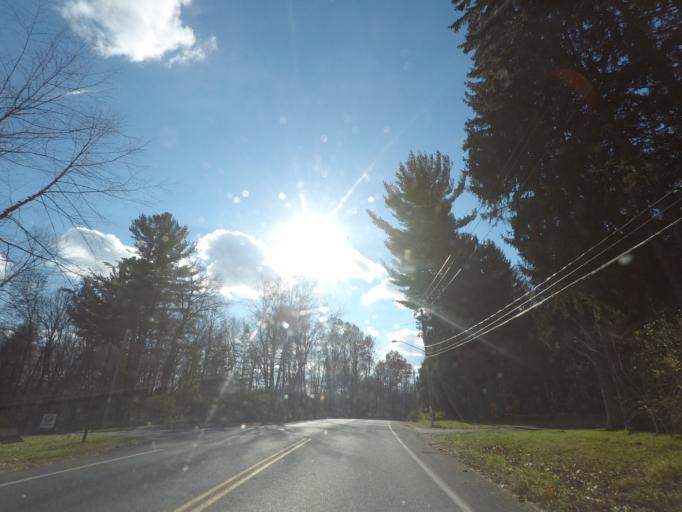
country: US
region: New York
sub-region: Saratoga County
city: Country Knolls
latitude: 42.8877
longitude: -73.7924
